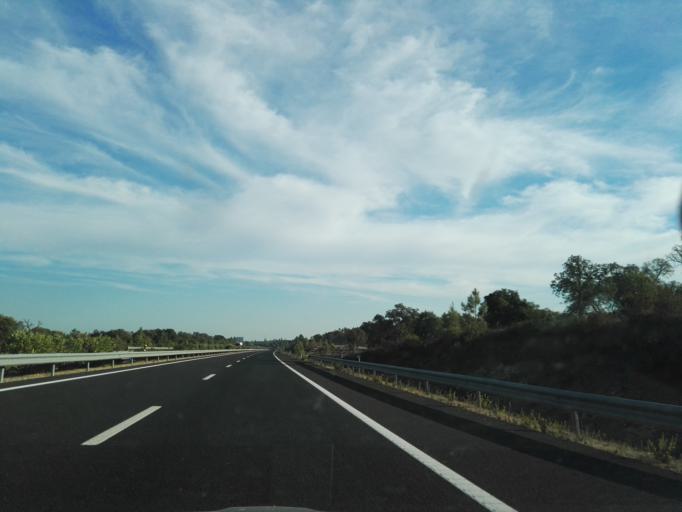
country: PT
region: Santarem
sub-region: Benavente
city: Poceirao
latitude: 38.8286
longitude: -8.7182
